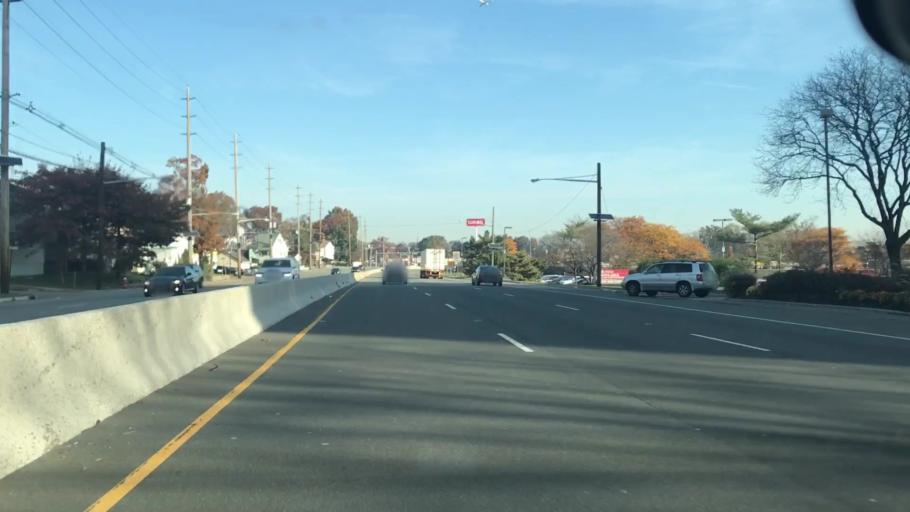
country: US
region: New Jersey
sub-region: Bergen County
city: Rutherford
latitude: 40.8181
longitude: -74.1021
